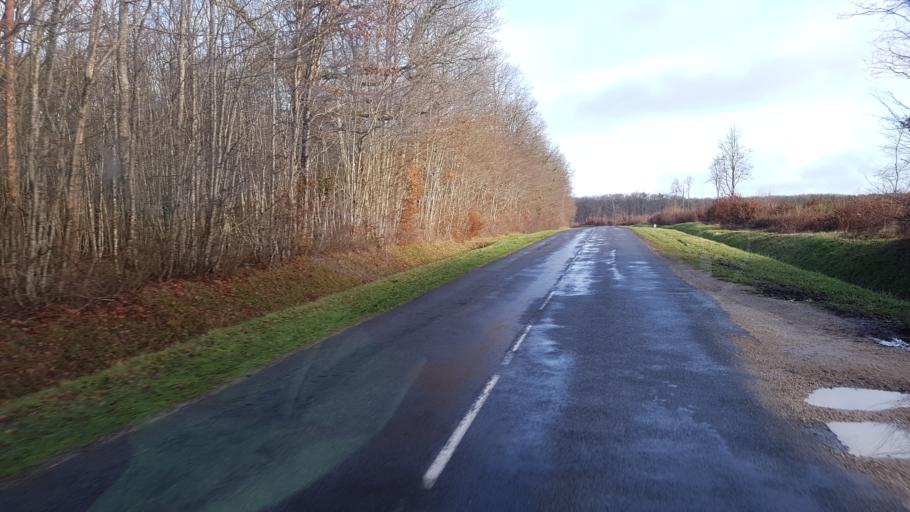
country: FR
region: Centre
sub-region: Departement du Loiret
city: Chilleurs-aux-Bois
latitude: 48.0175
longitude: 2.2043
